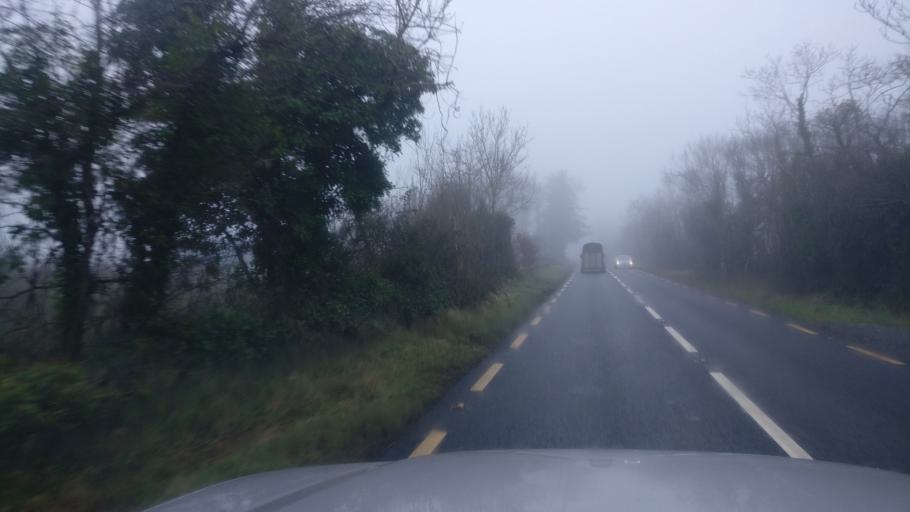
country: IE
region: Connaught
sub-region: County Galway
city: Loughrea
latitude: 53.1482
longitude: -8.6934
